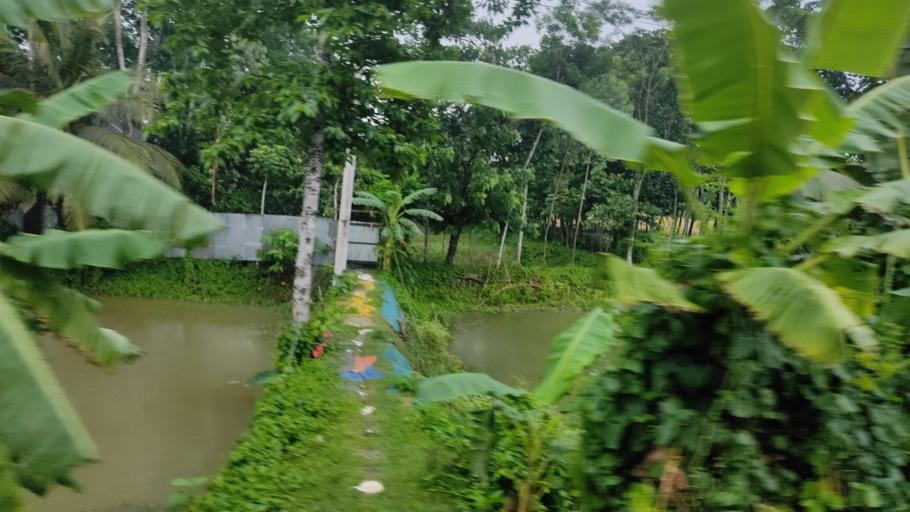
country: BD
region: Barisal
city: Bhandaria
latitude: 22.3127
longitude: 90.3252
